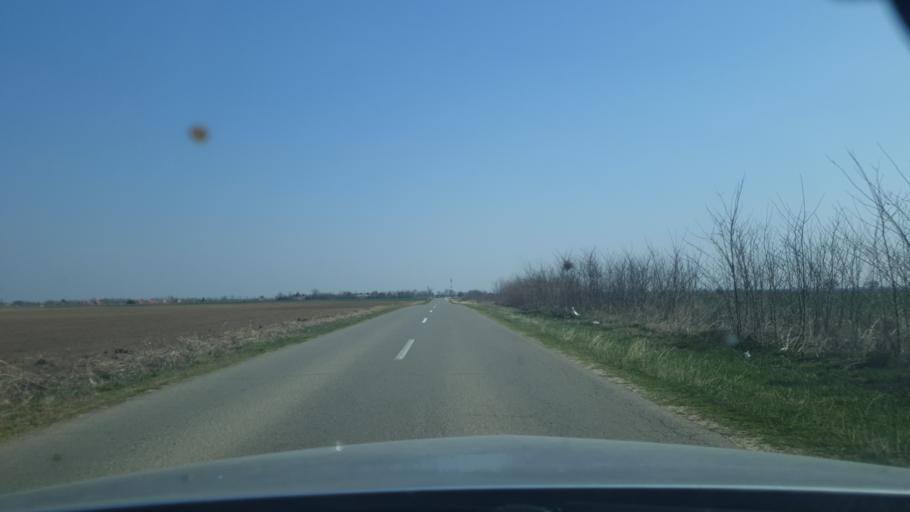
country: RS
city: Sasinci
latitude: 45.0478
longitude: 19.7075
